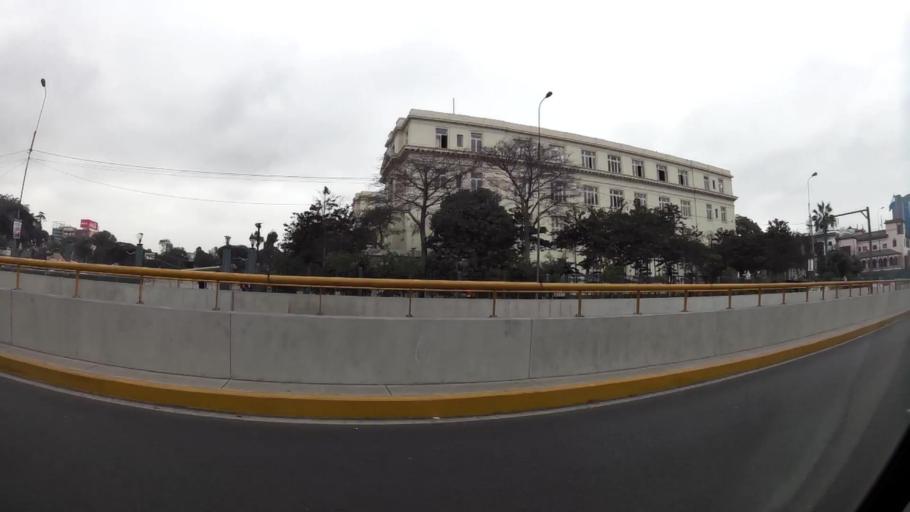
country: PE
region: Lima
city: Lima
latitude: -12.0634
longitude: -77.0378
